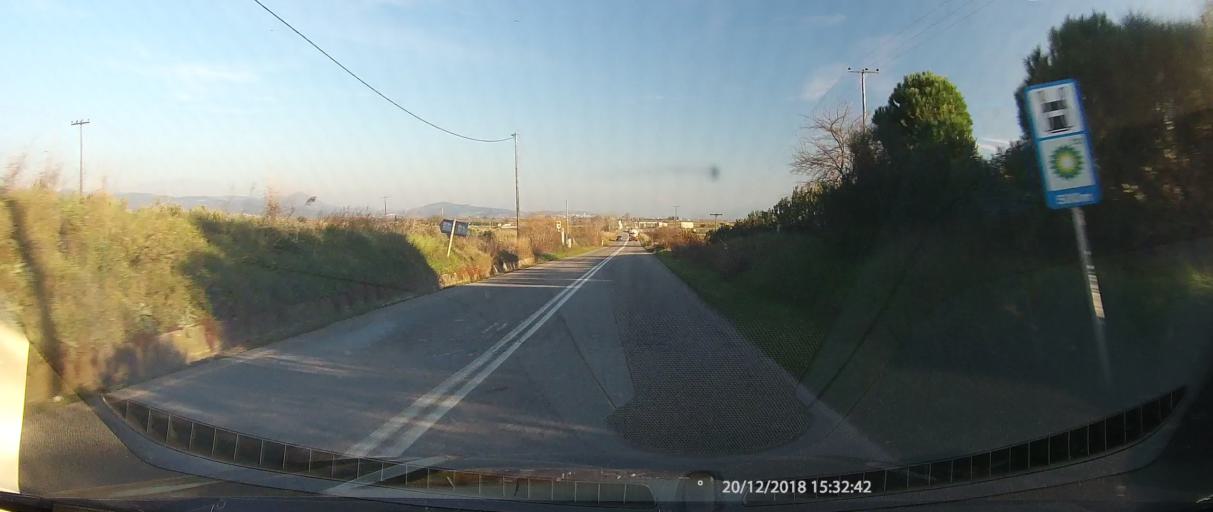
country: GR
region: Central Greece
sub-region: Nomos Fthiotidos
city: Lianokladhion
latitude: 38.9282
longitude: 22.2621
